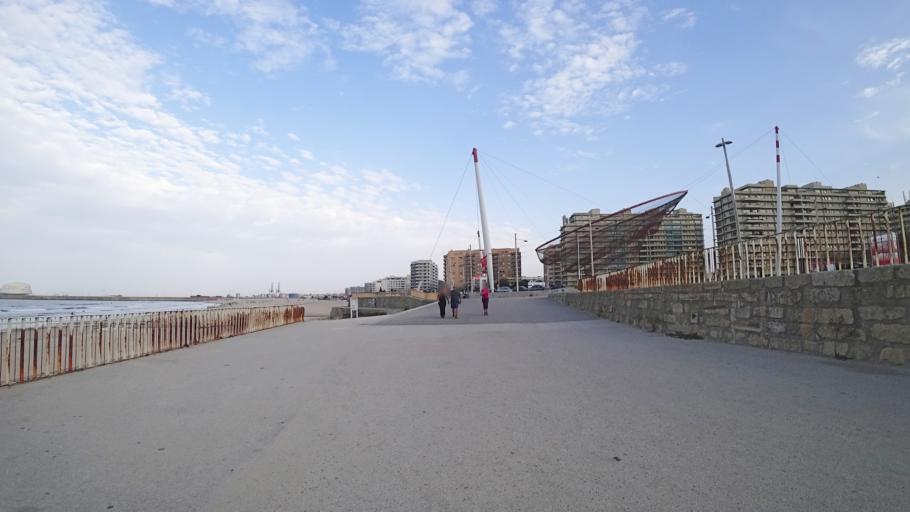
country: PT
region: Porto
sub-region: Matosinhos
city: Matosinhos
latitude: 41.1724
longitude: -8.6891
